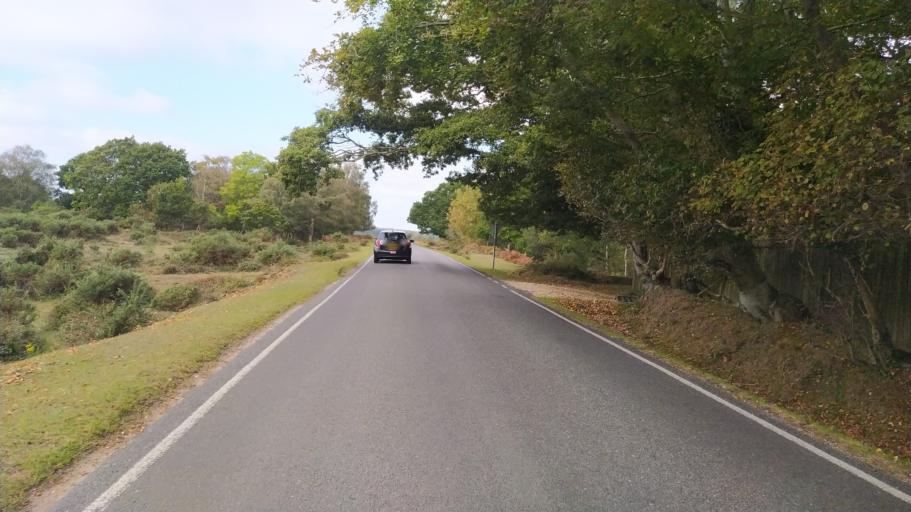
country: GB
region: England
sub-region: Hampshire
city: Brockenhurst
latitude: 50.7927
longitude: -1.5686
